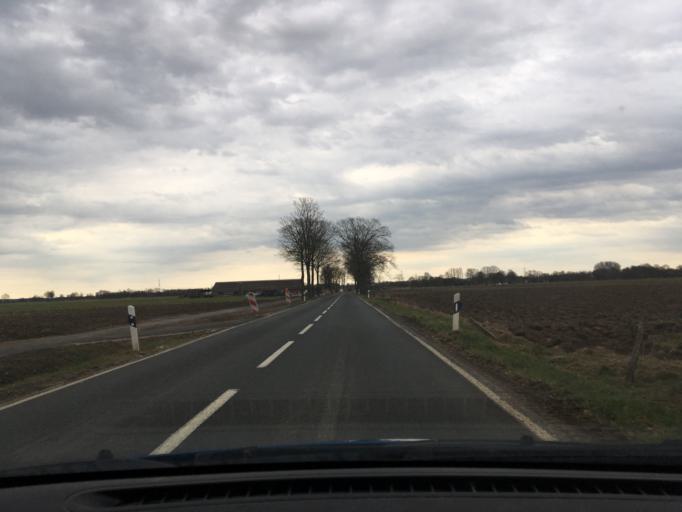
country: DE
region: Lower Saxony
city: Handorf
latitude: 53.3748
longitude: 10.3231
